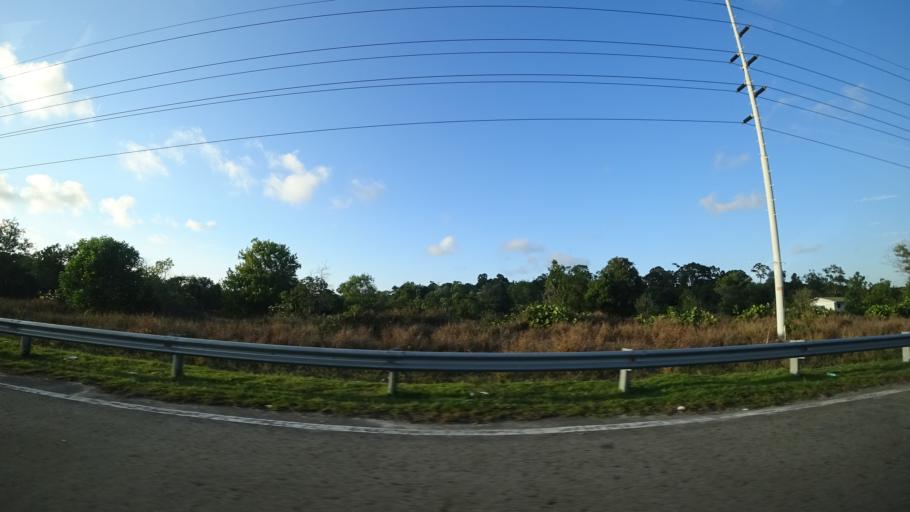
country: BN
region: Tutong
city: Tutong
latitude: 4.7525
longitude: 114.6286
